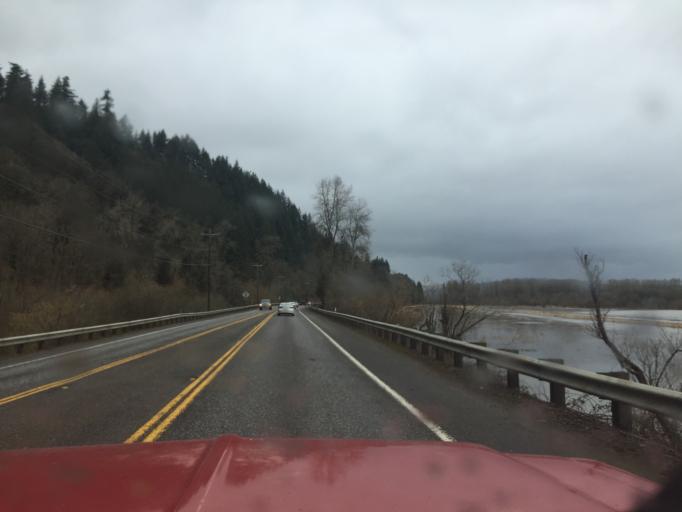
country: US
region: Oregon
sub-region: Columbia County
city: Rainier
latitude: 46.0485
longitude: -122.8982
